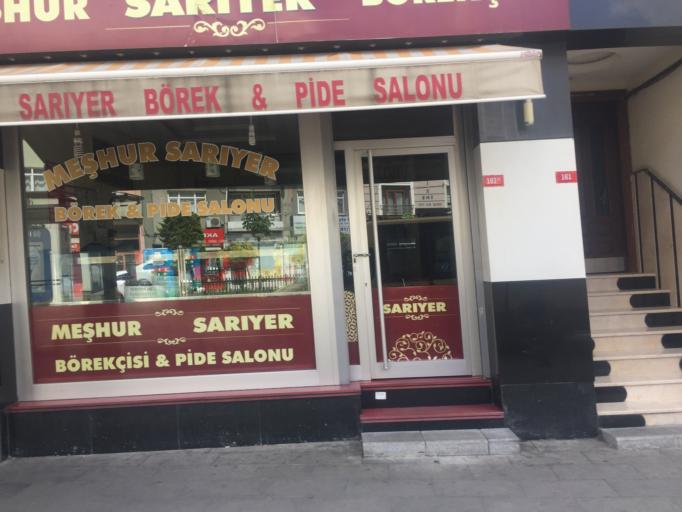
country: TR
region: Istanbul
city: Esenler
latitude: 41.0523
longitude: 28.9048
